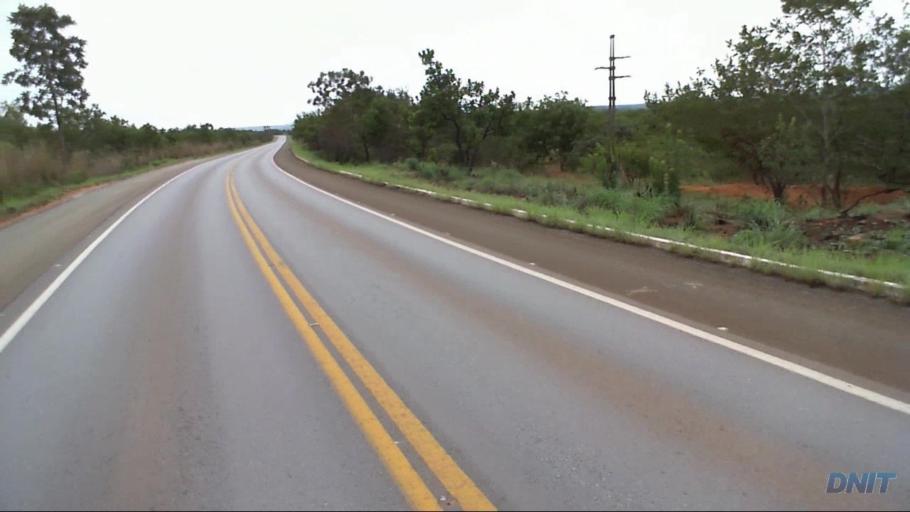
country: BR
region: Goias
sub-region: Barro Alto
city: Barro Alto
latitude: -14.7760
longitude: -49.0572
